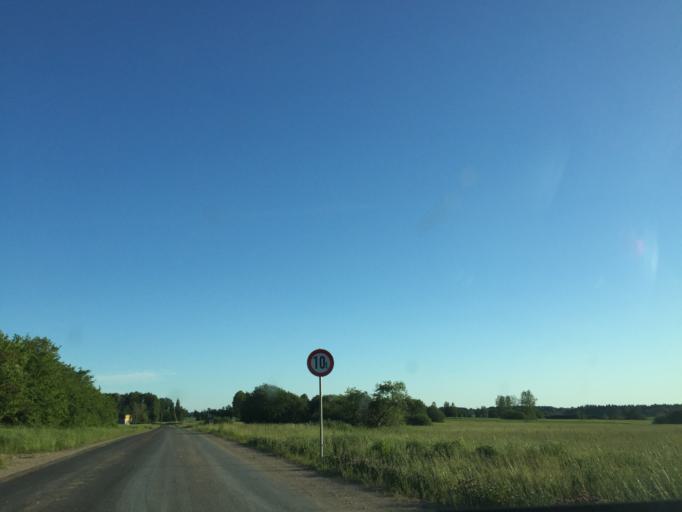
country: LV
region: Broceni
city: Broceni
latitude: 56.7726
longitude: 22.5359
